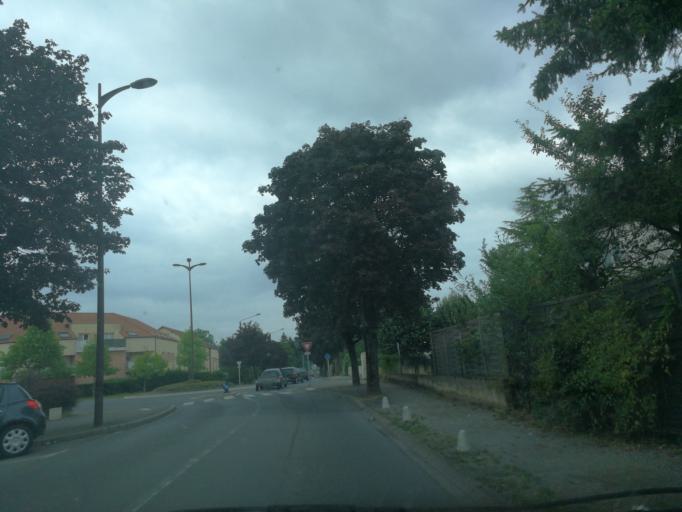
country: FR
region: Lorraine
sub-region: Departement de la Moselle
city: Terville
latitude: 49.3629
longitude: 6.1403
